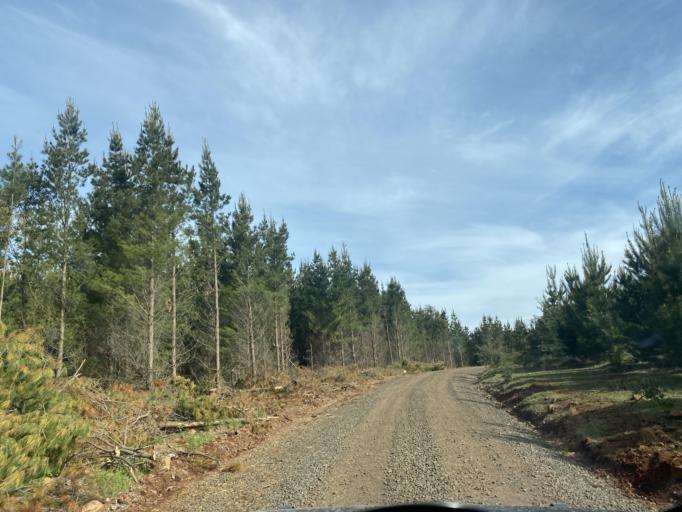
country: AU
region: Victoria
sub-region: Mansfield
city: Mansfield
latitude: -36.8324
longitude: 146.1796
